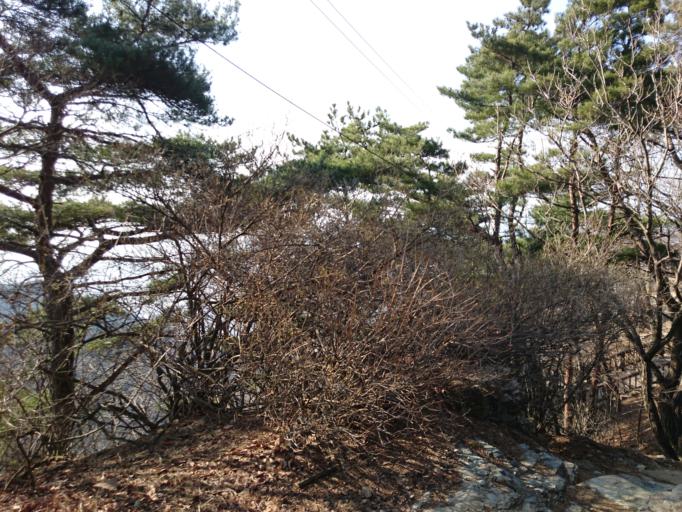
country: KR
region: Daegu
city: Daegu
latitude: 35.8218
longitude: 128.5792
